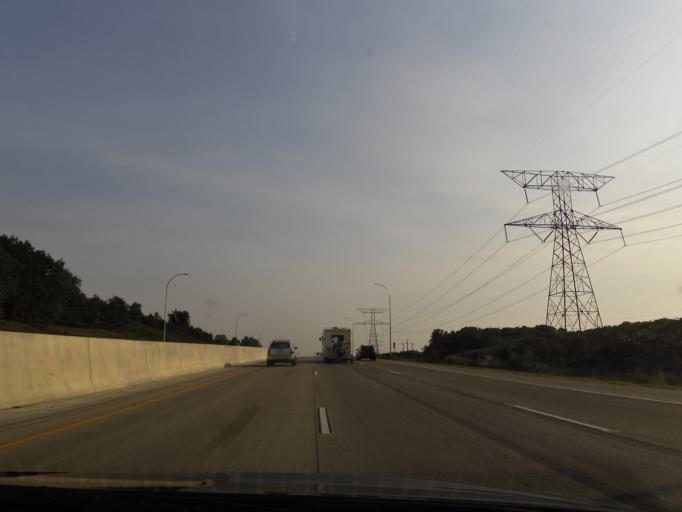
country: US
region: Minnesota
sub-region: Hennepin County
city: Plymouth
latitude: 45.0367
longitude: -93.4529
